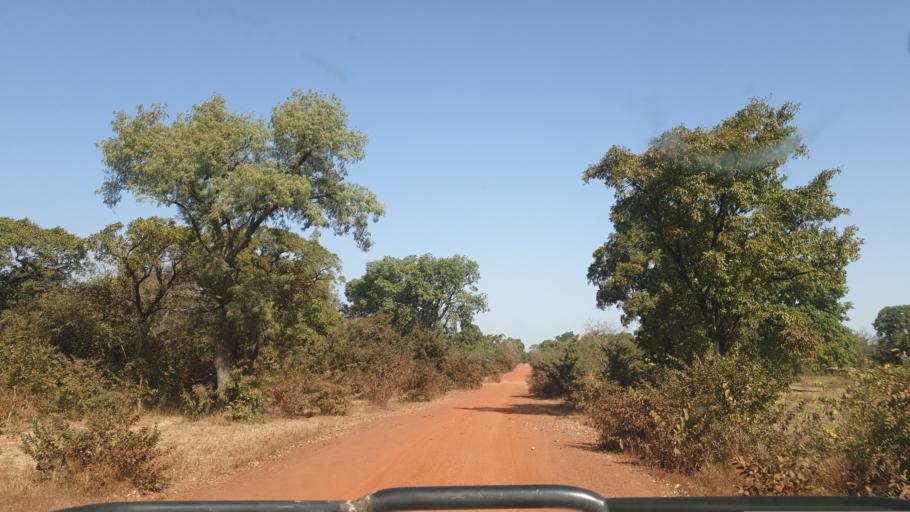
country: ML
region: Sikasso
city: Bougouni
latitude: 11.8387
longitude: -6.9783
